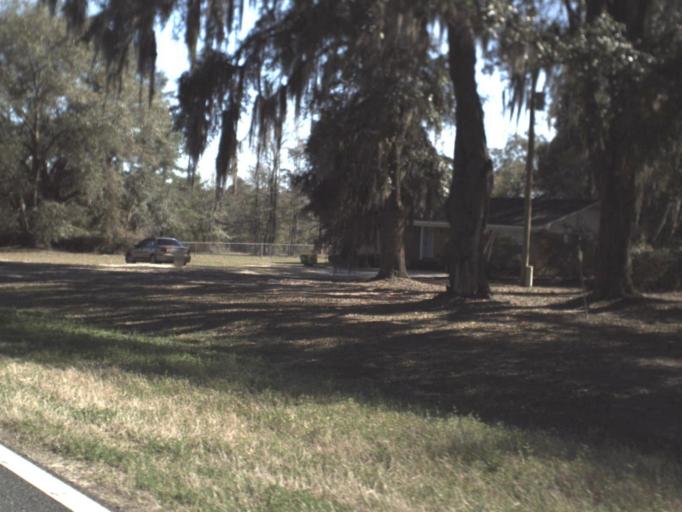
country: US
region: Florida
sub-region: Gadsden County
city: Quincy
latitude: 30.5564
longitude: -84.5309
